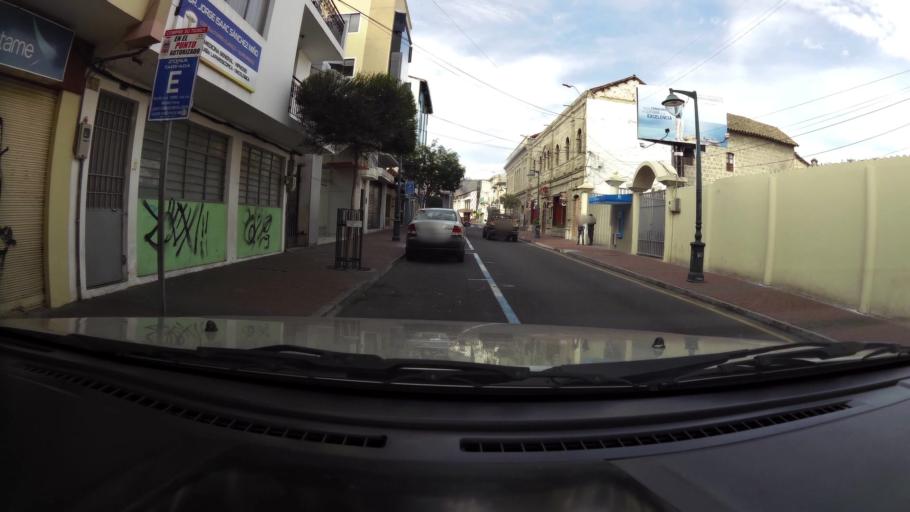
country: EC
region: Tungurahua
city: Ambato
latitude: -1.2361
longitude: -78.6273
